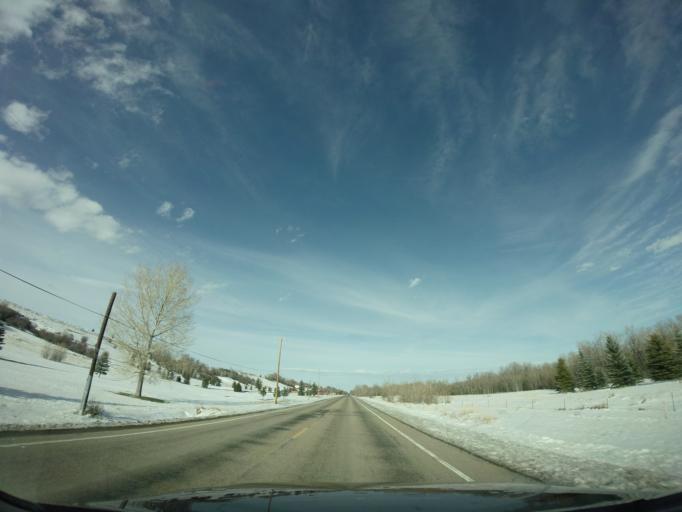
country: US
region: Montana
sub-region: Carbon County
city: Red Lodge
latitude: 45.2077
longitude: -109.2440
